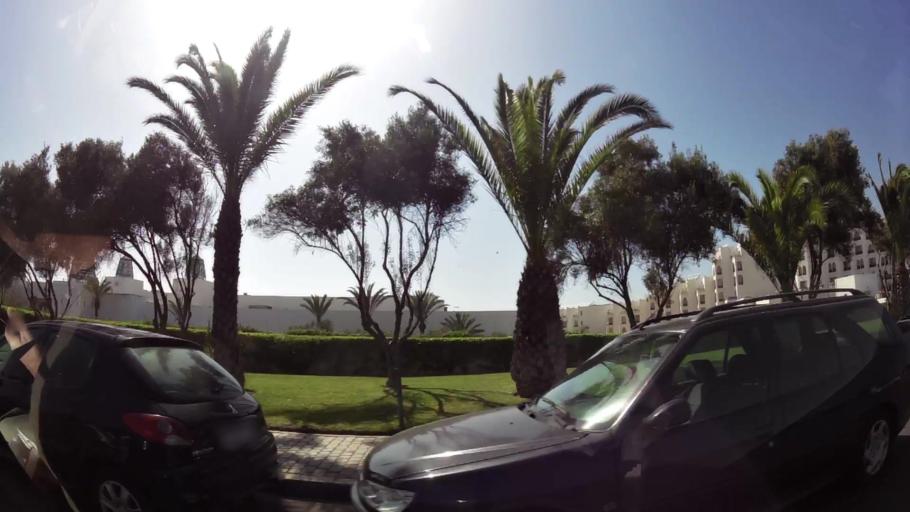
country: MA
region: Souss-Massa-Draa
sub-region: Agadir-Ida-ou-Tnan
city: Agadir
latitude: 30.3938
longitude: -9.5960
